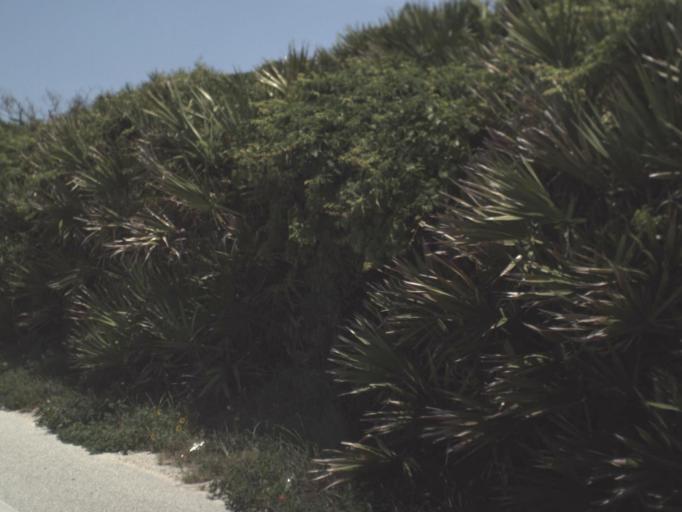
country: US
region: Florida
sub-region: Saint Johns County
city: Villano Beach
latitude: 29.9401
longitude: -81.3005
